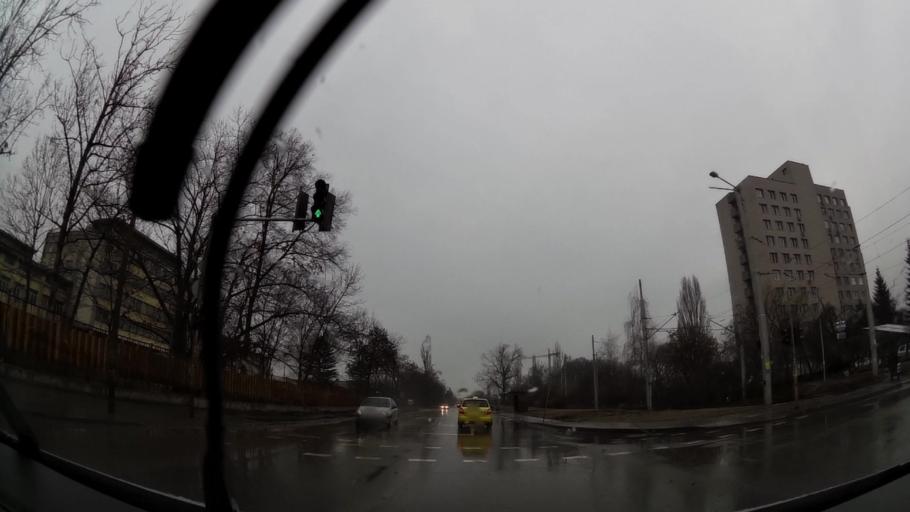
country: BG
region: Sofia-Capital
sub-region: Stolichna Obshtina
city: Sofia
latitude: 42.6681
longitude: 23.4023
